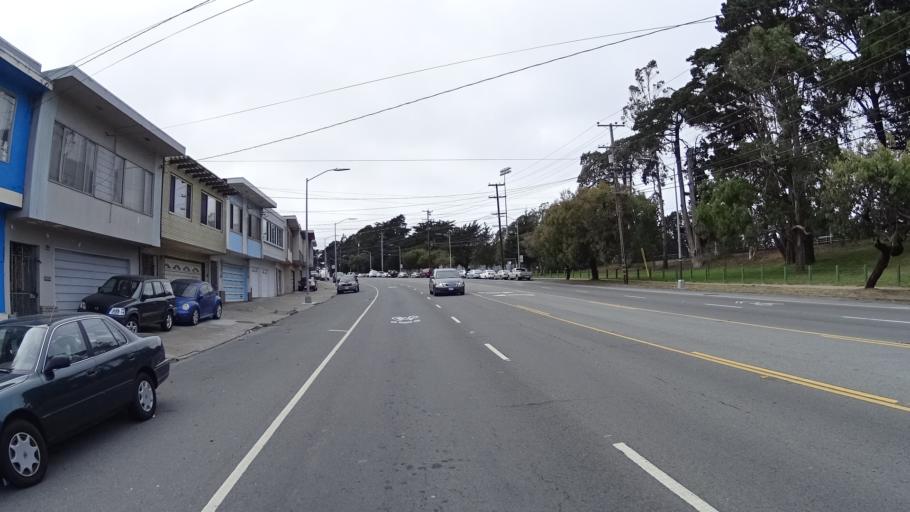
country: US
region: California
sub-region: San Mateo County
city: Daly City
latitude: 37.7118
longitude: -122.4284
